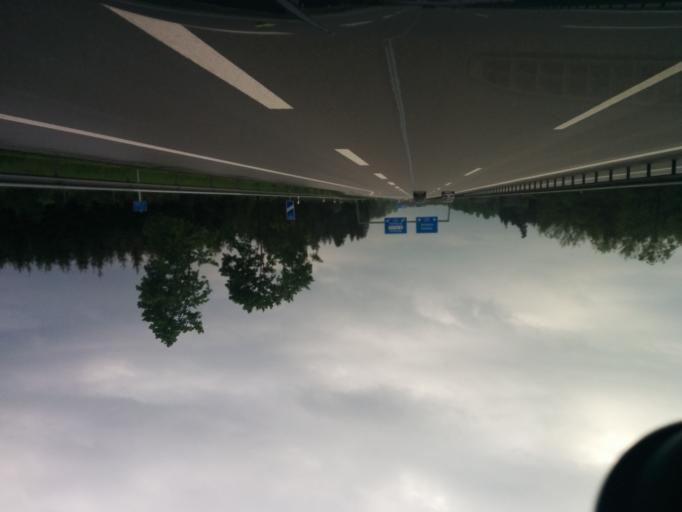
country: DE
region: Bavaria
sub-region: Upper Bavaria
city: Ottobrunn
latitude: 48.0341
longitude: 11.6540
